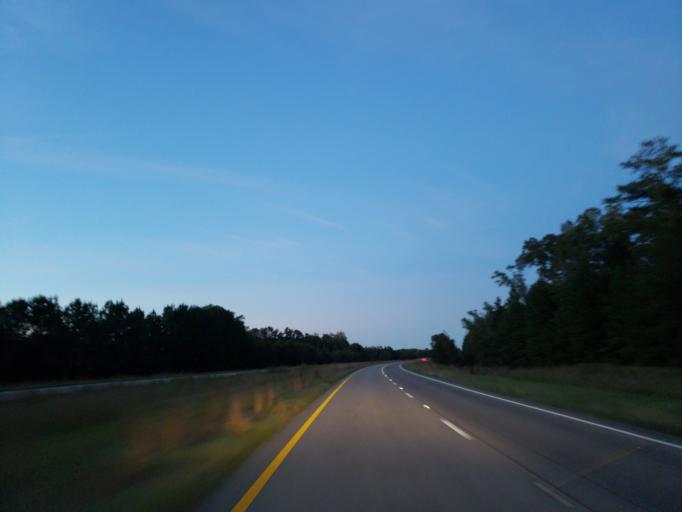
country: US
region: Mississippi
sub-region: Clarke County
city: Quitman
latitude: 31.8609
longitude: -88.7201
